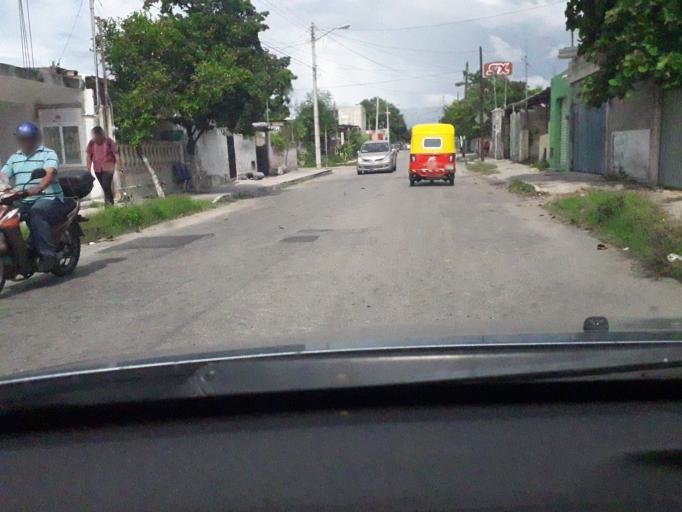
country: MX
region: Yucatan
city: Merida
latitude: 20.9668
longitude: -89.6600
